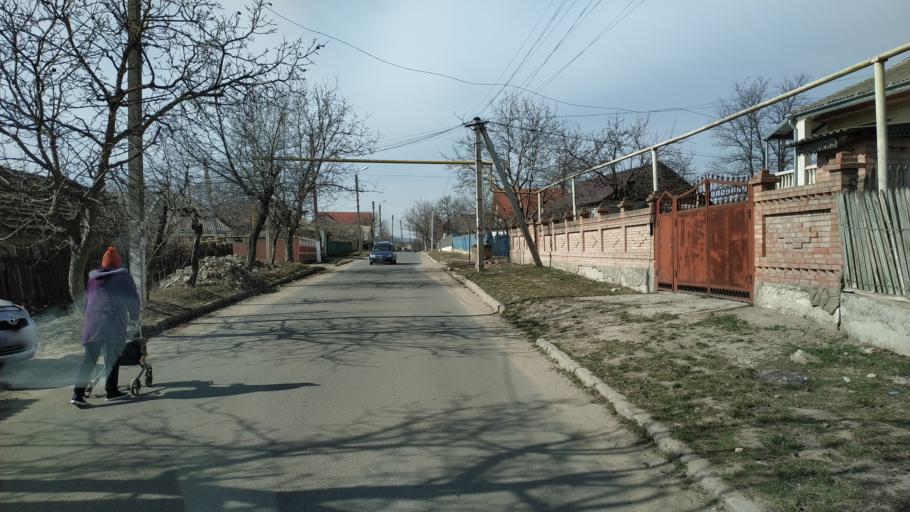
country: MD
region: Straseni
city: Straseni
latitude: 47.0955
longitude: 28.6600
